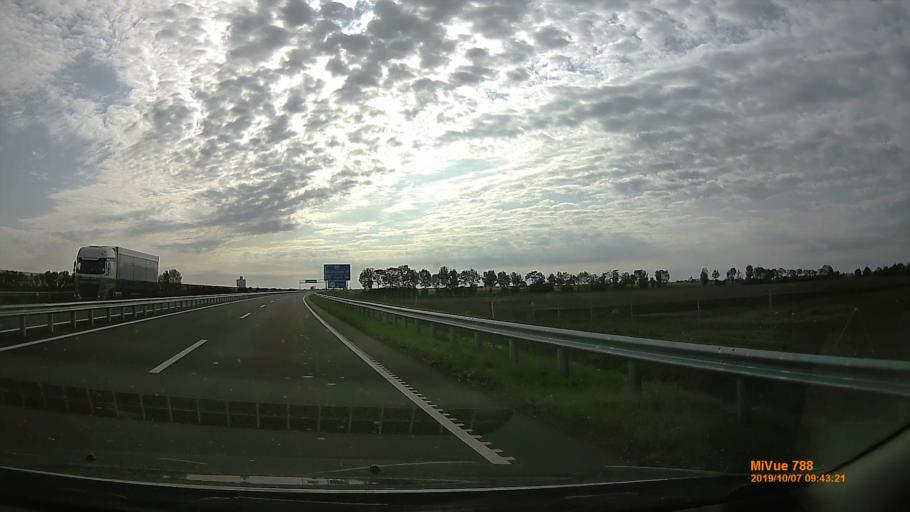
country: HU
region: Bekes
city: Kondoros
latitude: 46.8075
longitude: 20.6880
